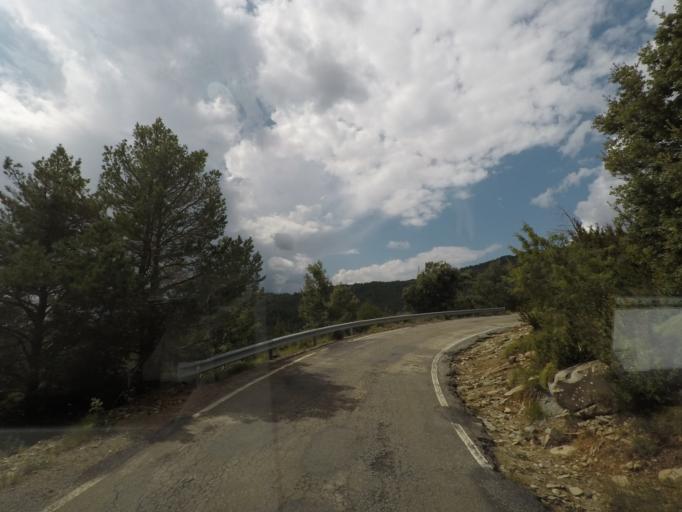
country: ES
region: Aragon
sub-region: Provincia de Huesca
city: Boltana
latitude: 42.4029
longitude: -0.0177
